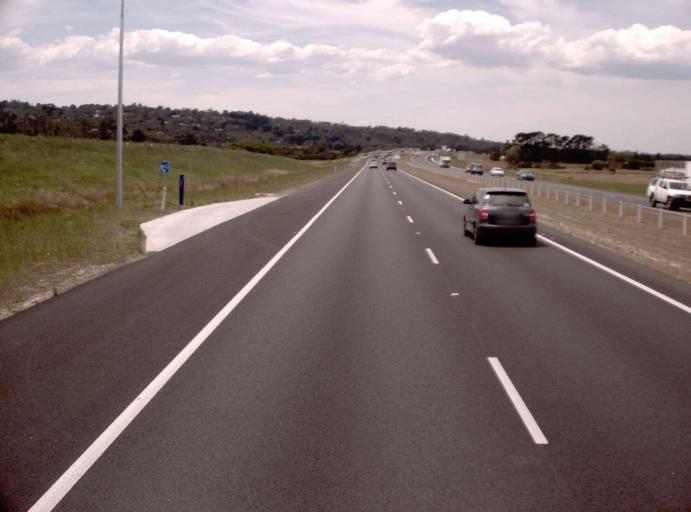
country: AU
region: Victoria
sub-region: Mornington Peninsula
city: Moorooduc
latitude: -38.2146
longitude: 145.1295
